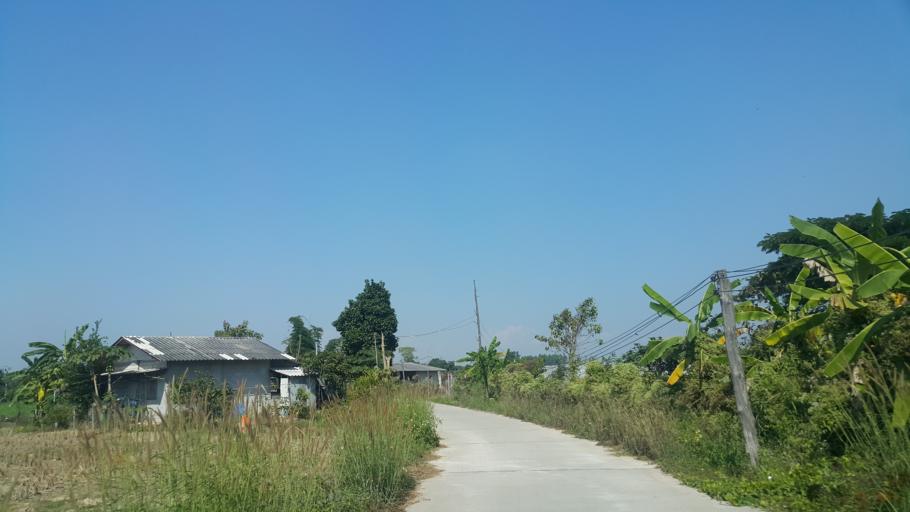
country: TH
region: Chiang Mai
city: San Kamphaeng
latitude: 18.6899
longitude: 99.1668
